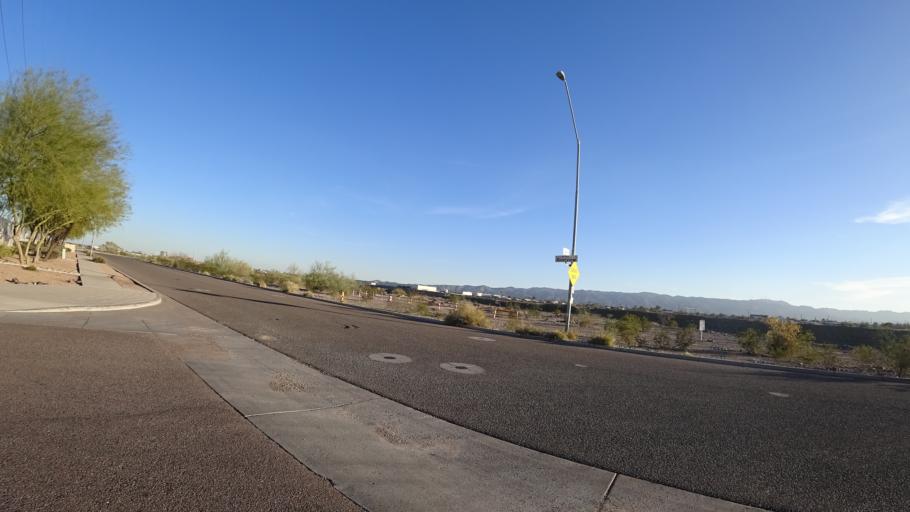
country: US
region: Arizona
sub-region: Maricopa County
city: Phoenix
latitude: 33.4183
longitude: -112.0429
